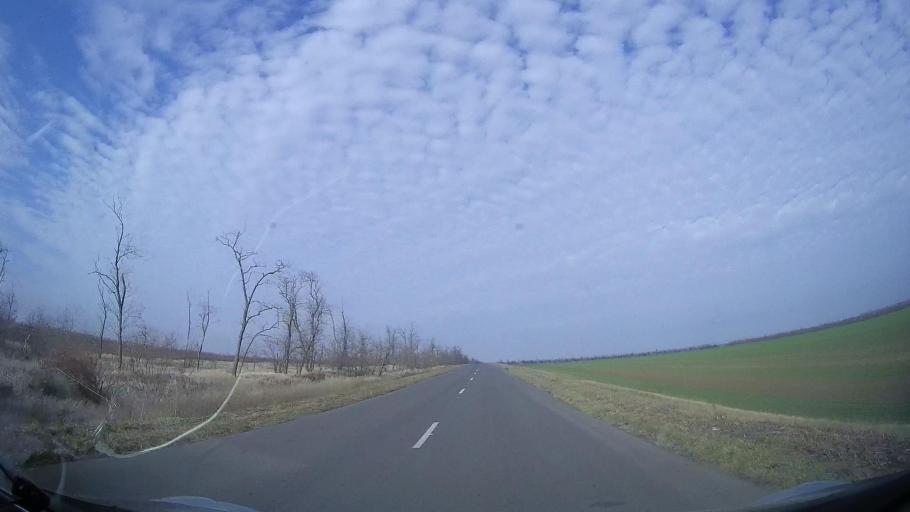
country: RU
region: Rostov
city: Gigant
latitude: 46.8527
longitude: 41.2837
